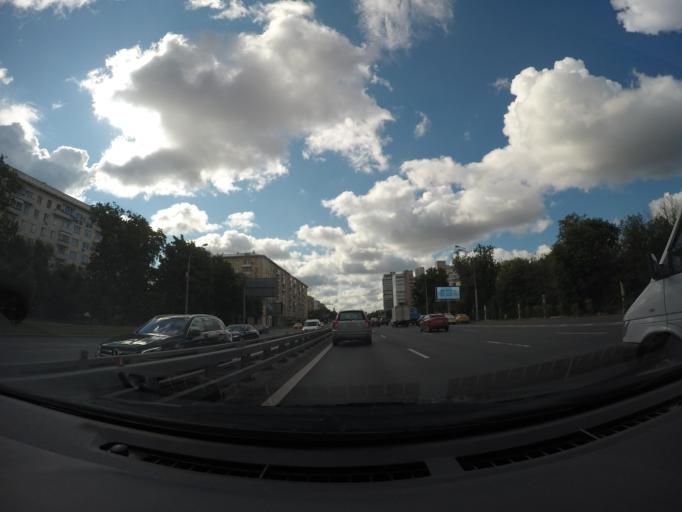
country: RU
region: Moskovskaya
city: Levoberezhnyy
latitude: 55.8349
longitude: 37.4847
